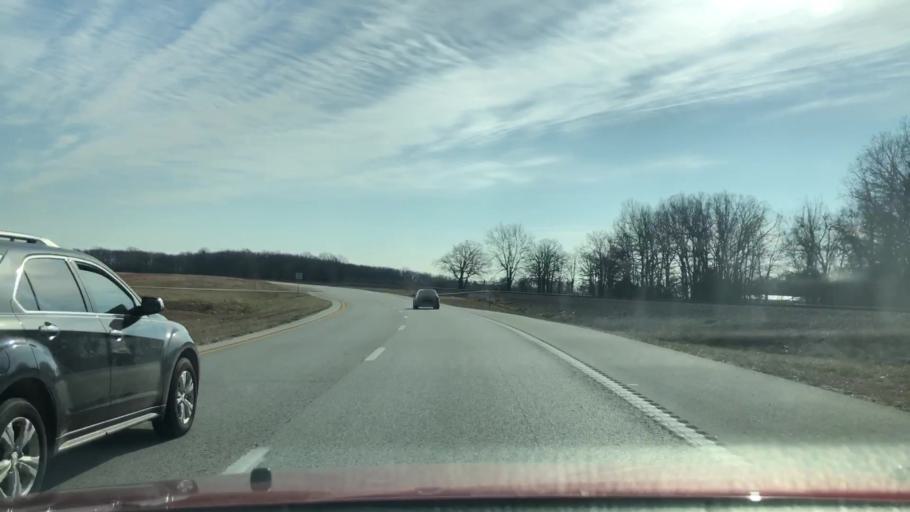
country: US
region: Missouri
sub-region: Webster County
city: Seymour
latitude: 37.1328
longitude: -92.7416
